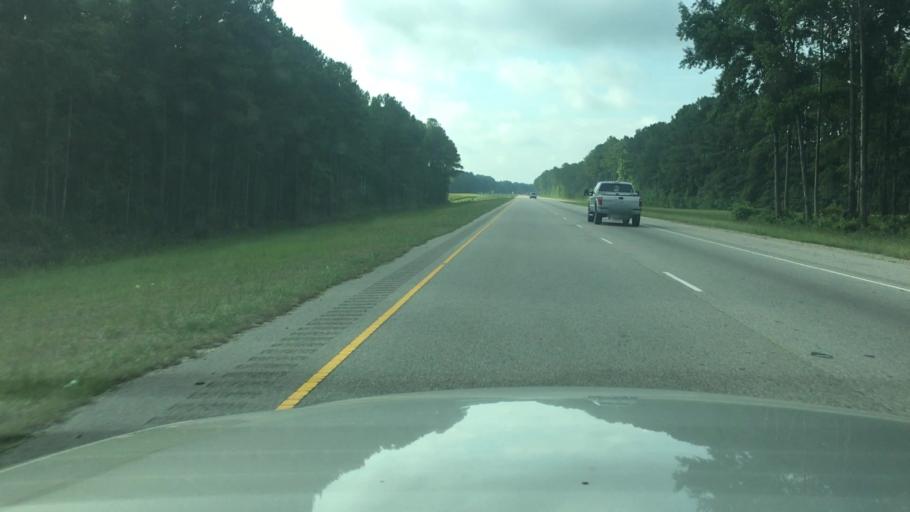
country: US
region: North Carolina
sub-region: Cumberland County
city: Fayetteville
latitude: 34.9744
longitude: -78.8554
